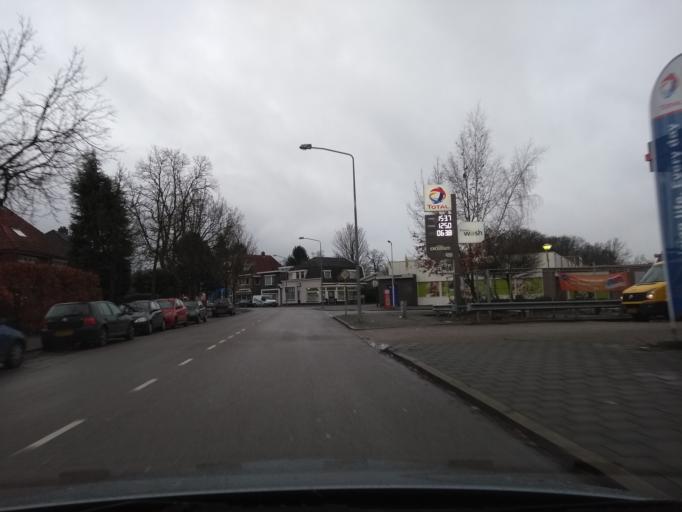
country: NL
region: Overijssel
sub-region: Gemeente Almelo
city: Almelo
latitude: 52.3692
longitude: 6.6671
